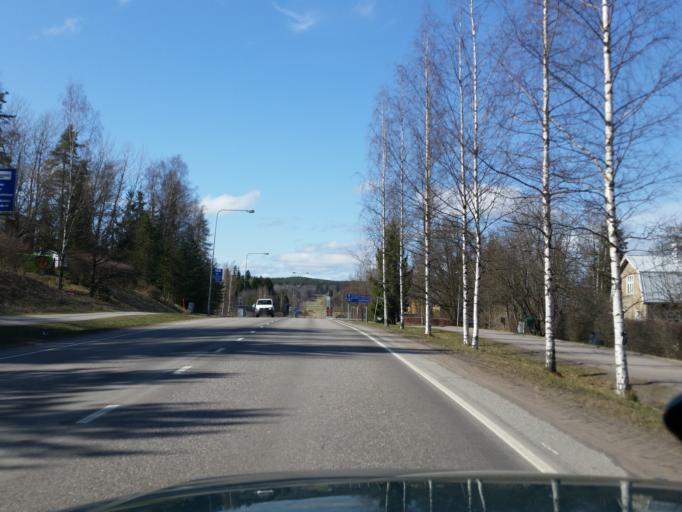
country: FI
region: Uusimaa
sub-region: Helsinki
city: Vihti
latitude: 60.4147
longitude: 24.3288
